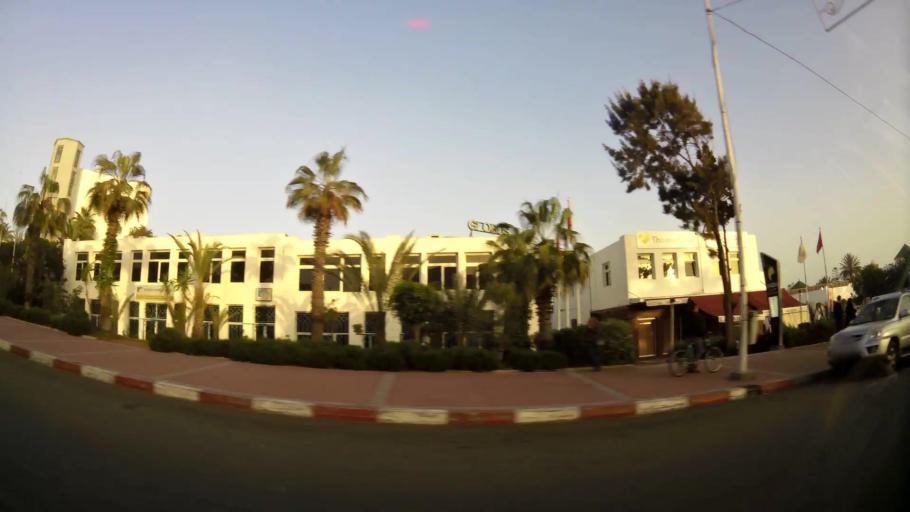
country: MA
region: Souss-Massa-Draa
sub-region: Agadir-Ida-ou-Tnan
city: Agadir
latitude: 30.4079
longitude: -9.5971
